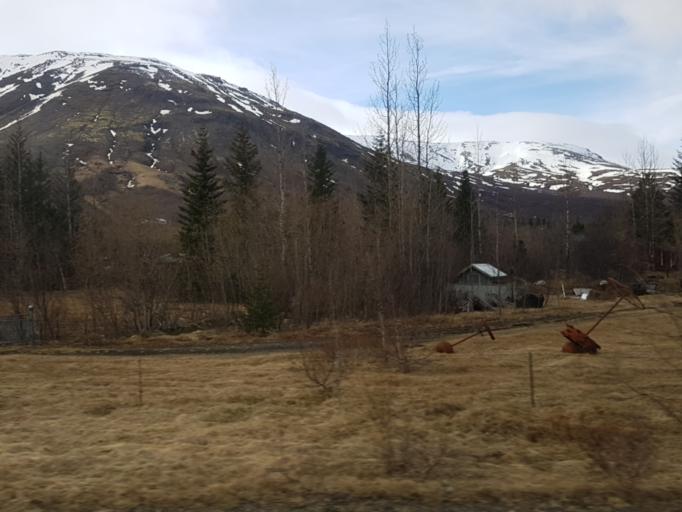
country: IS
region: South
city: Selfoss
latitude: 64.2360
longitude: -20.7052
